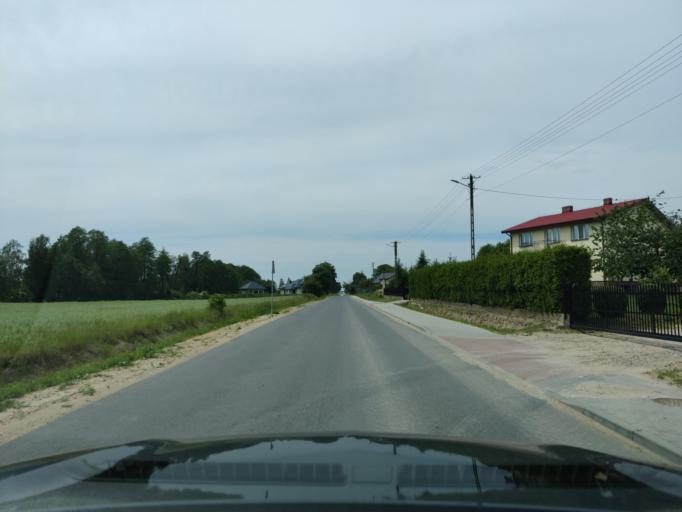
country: PL
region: Masovian Voivodeship
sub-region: Powiat pultuski
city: Obryte
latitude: 52.7238
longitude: 21.3069
